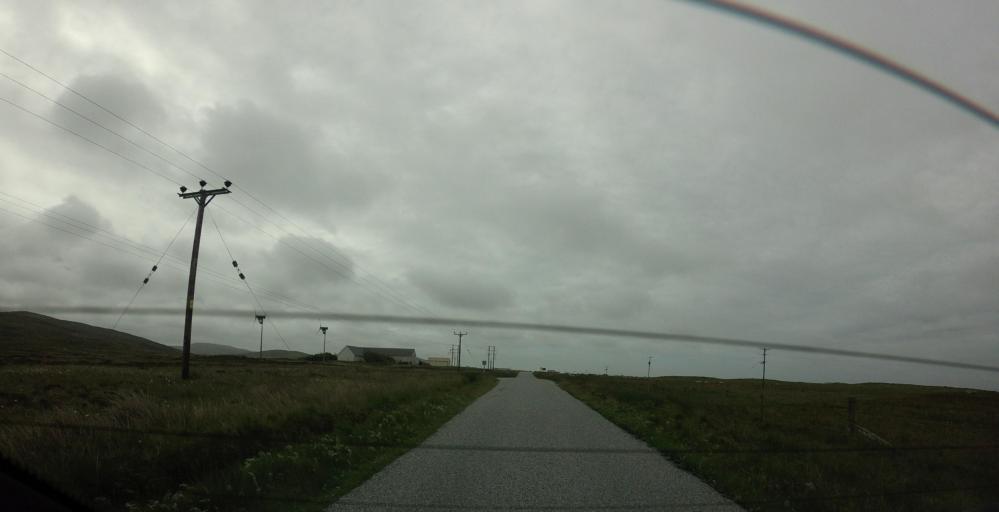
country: GB
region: Scotland
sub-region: Eilean Siar
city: Isle of South Uist
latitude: 57.2237
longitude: -7.3968
